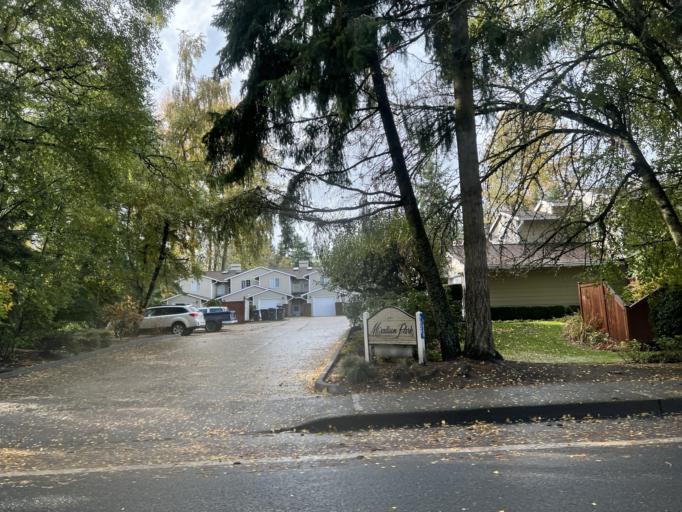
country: US
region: Washington
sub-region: Kitsap County
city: Bainbridge Island
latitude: 47.6337
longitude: -122.5210
